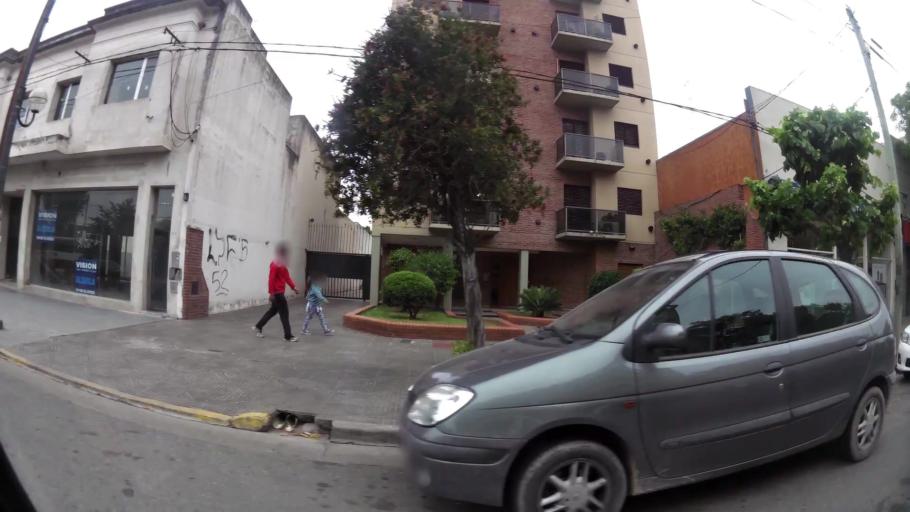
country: AR
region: Buenos Aires
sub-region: Partido de La Plata
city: La Plata
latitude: -34.9290
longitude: -57.9752
